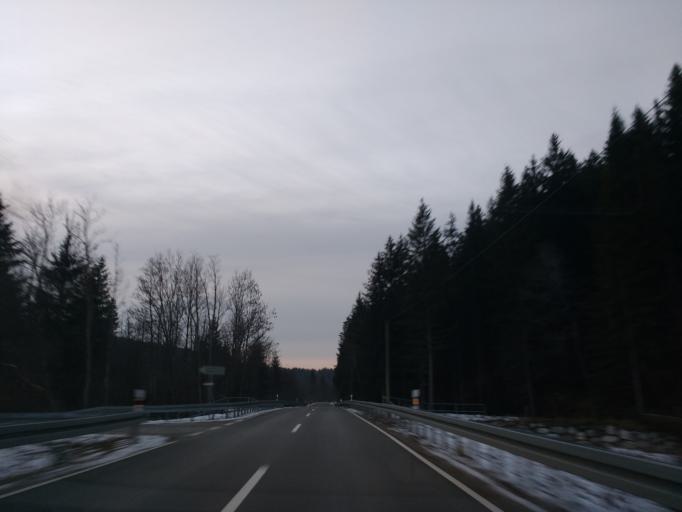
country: DE
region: Bavaria
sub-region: Swabia
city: Halblech
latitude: 47.6470
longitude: 10.8068
